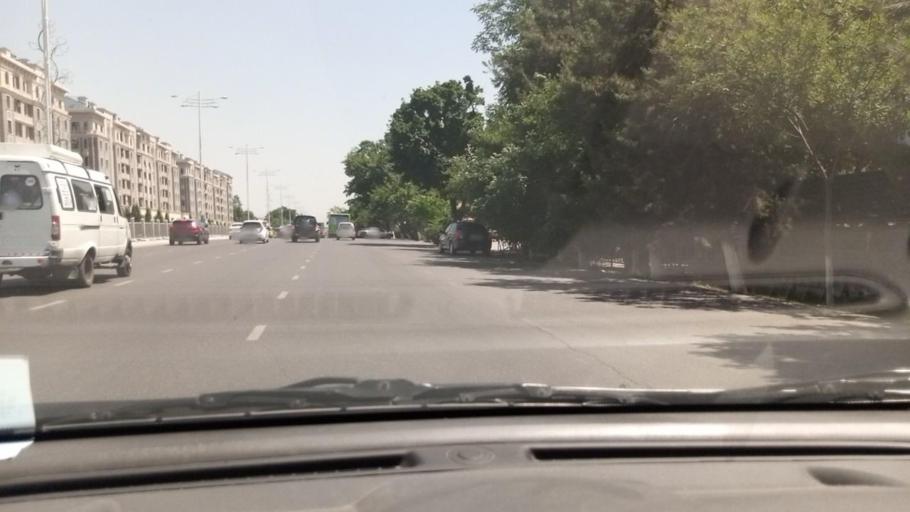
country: UZ
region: Toshkent Shahri
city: Tashkent
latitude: 41.2904
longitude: 69.2257
